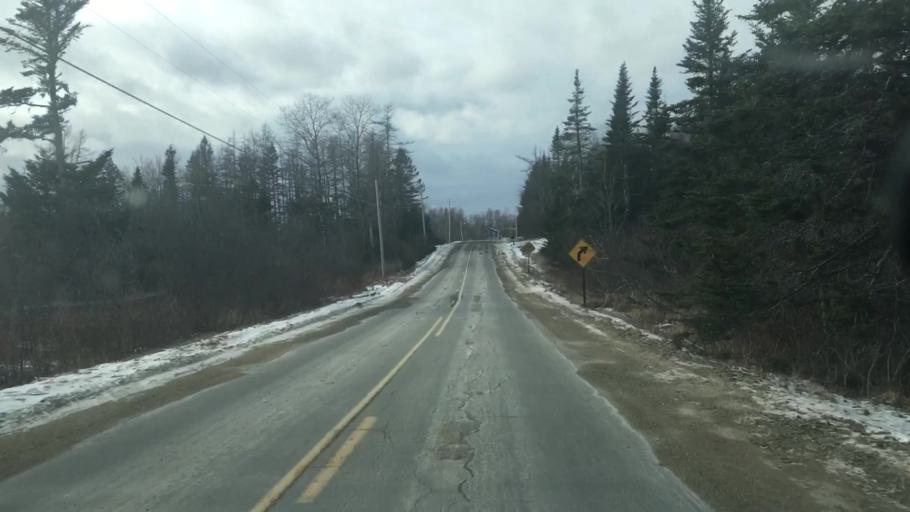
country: US
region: Maine
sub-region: Washington County
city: Machias
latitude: 44.6560
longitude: -67.5265
